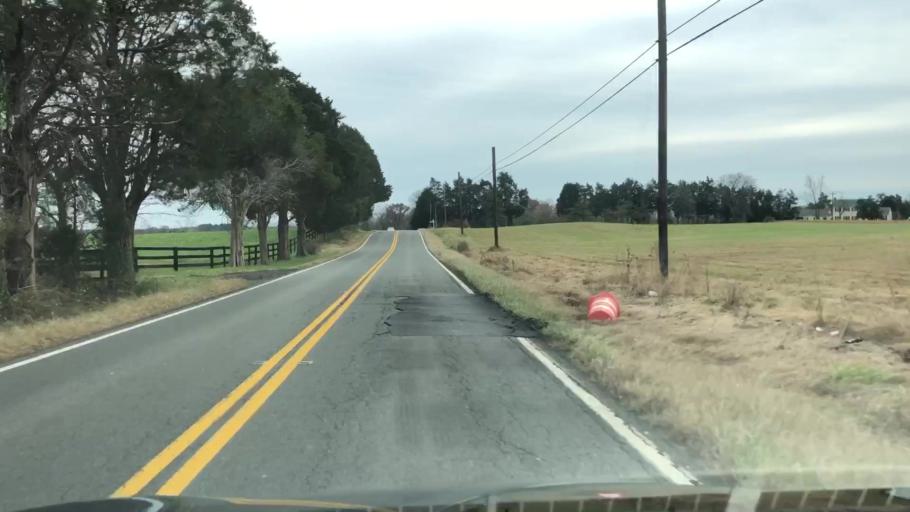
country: US
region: Virginia
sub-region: Fauquier County
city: New Baltimore
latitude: 38.7594
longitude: -77.6780
